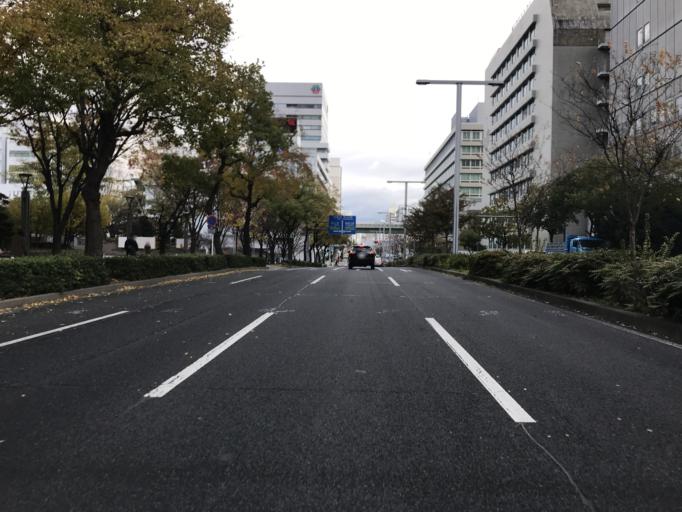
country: JP
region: Aichi
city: Nagoya-shi
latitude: 35.1702
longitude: 136.9116
